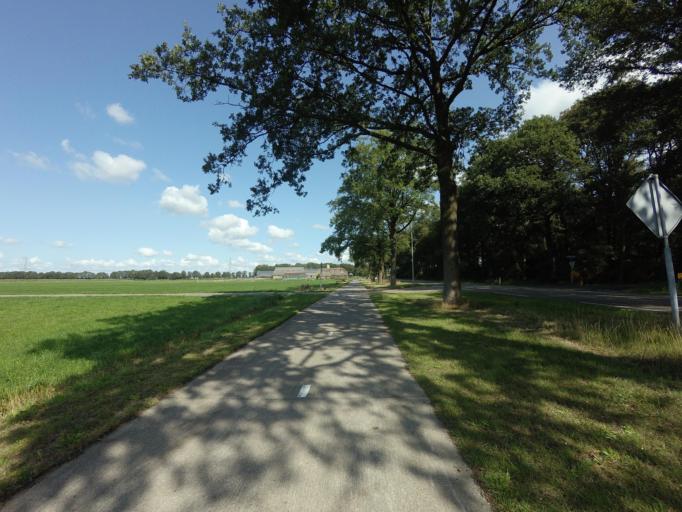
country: NL
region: Overijssel
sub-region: Gemeente Dalfsen
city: Dalfsen
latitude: 52.5357
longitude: 6.2614
